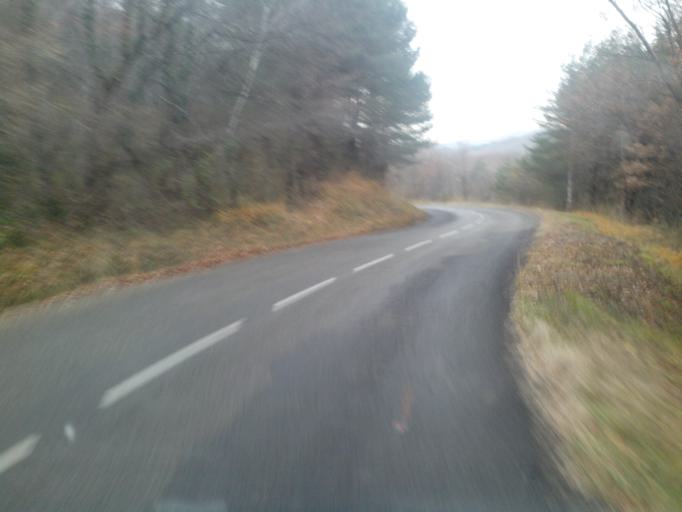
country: FR
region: Midi-Pyrenees
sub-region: Departement de l'Ariege
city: Varilhes
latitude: 43.0332
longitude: 1.5403
